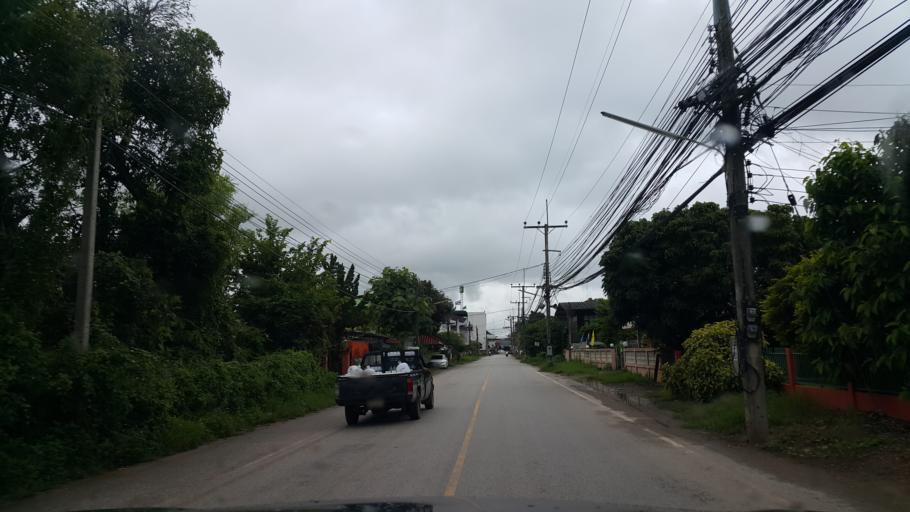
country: TH
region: Phayao
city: Chiang Kham
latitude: 19.5260
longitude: 100.3069
